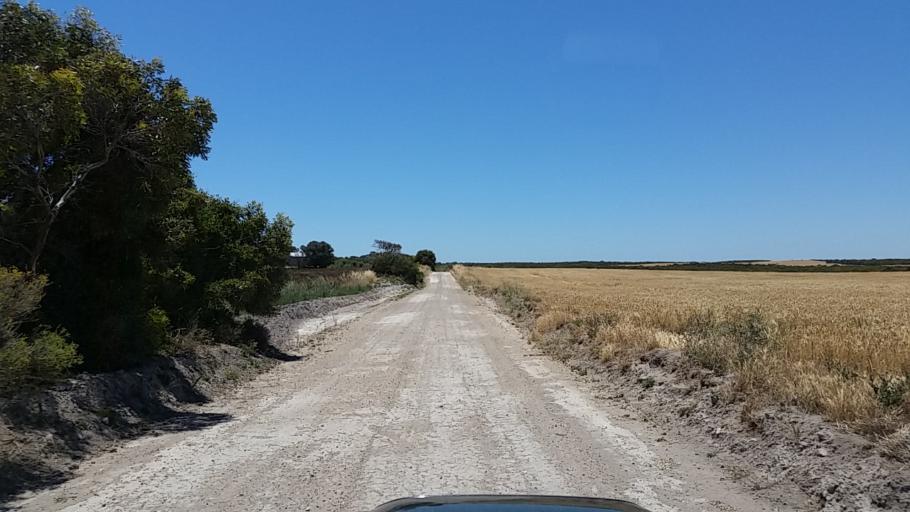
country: AU
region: South Australia
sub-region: Yorke Peninsula
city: Honiton
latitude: -35.2342
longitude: 137.1256
